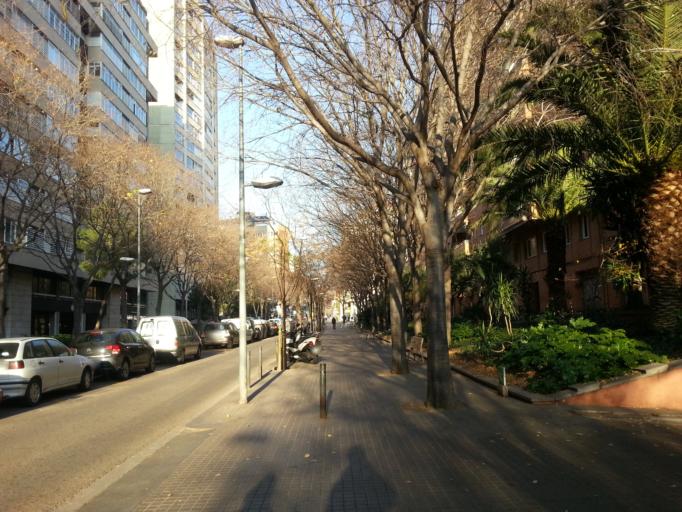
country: ES
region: Catalonia
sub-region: Provincia de Barcelona
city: Sants-Montjuic
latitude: 41.3801
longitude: 2.1456
